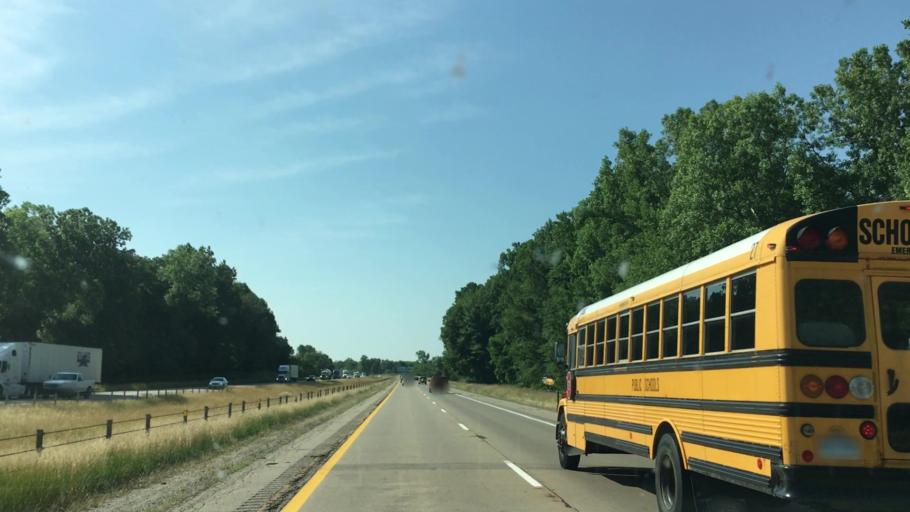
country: US
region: Michigan
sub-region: Ionia County
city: Portland
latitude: 42.8353
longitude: -84.8442
